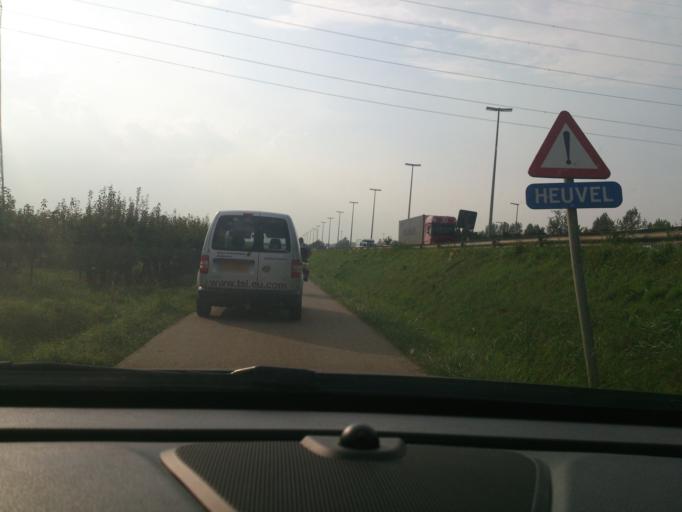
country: BE
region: Flanders
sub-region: Provincie Oost-Vlaanderen
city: Beveren
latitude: 51.2420
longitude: 4.2561
